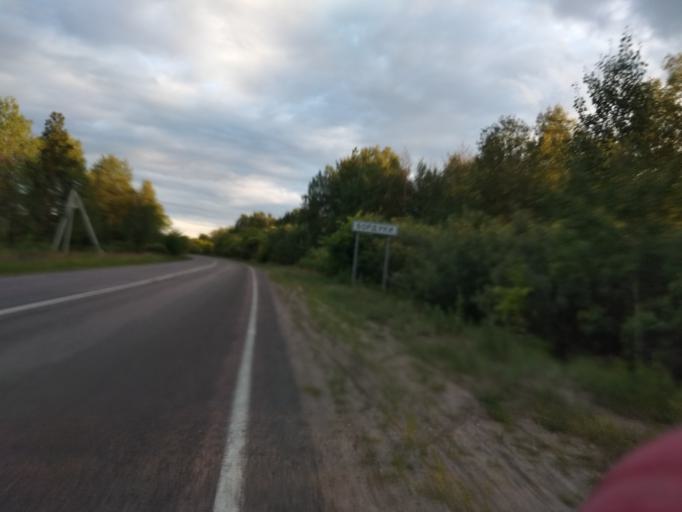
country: RU
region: Moskovskaya
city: Misheronskiy
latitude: 55.6050
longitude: 39.7090
